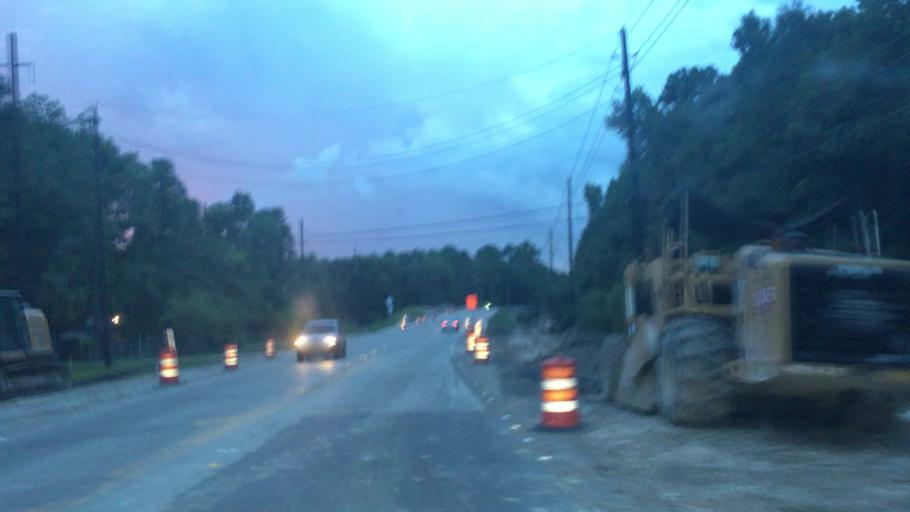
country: US
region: Texas
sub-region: Harris County
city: Humble
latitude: 29.9495
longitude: -95.2497
